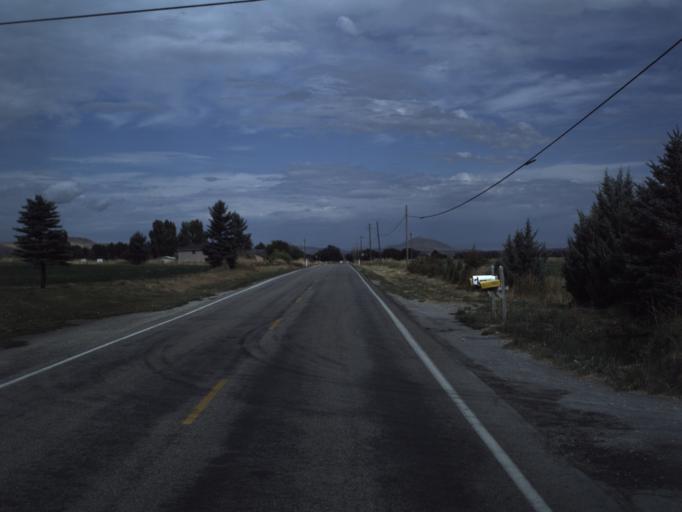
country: US
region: Utah
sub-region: Cache County
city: Mendon
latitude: 41.7211
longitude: -111.9790
